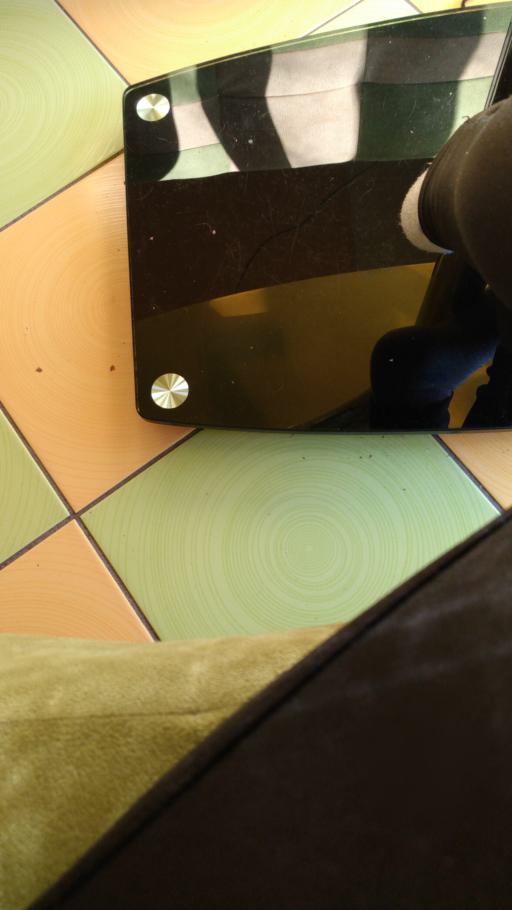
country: RU
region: Moskovskaya
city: Pervomayskiy
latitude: 55.1118
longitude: 38.6666
